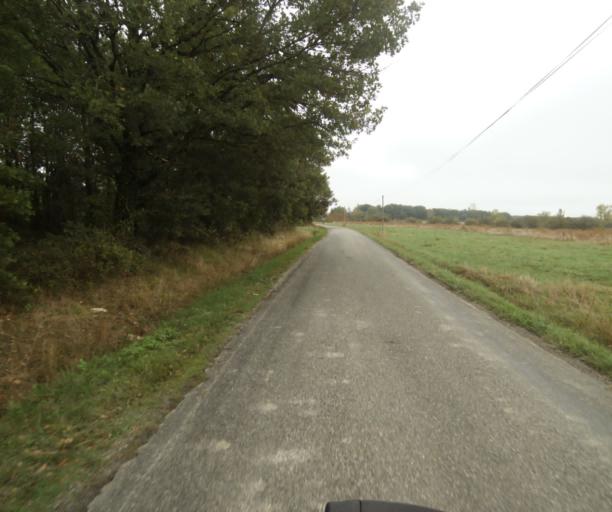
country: FR
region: Midi-Pyrenees
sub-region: Departement du Tarn-et-Garonne
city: Orgueil
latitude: 43.8954
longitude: 1.3903
